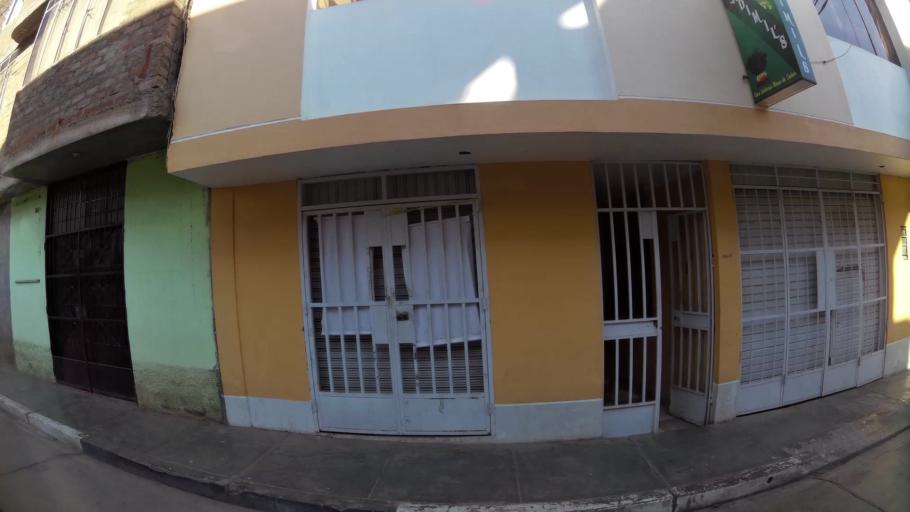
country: PE
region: Junin
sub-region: Provincia de Huancayo
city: El Tambo
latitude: -12.0575
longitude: -75.2276
